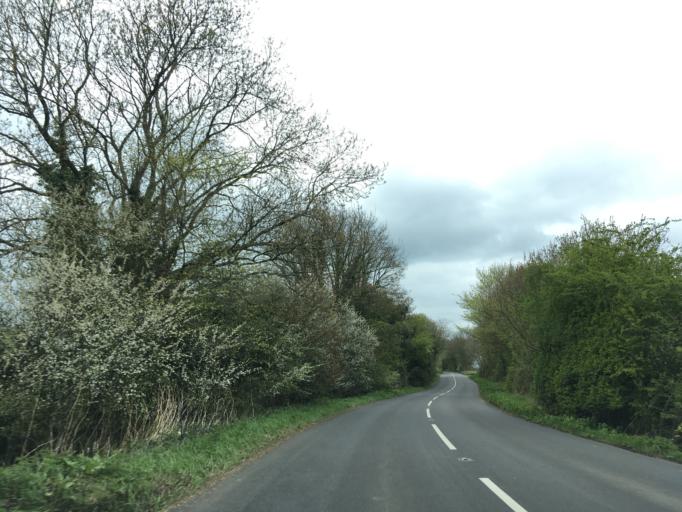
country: GB
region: England
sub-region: Gloucestershire
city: Nailsworth
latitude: 51.6880
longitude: -2.2774
